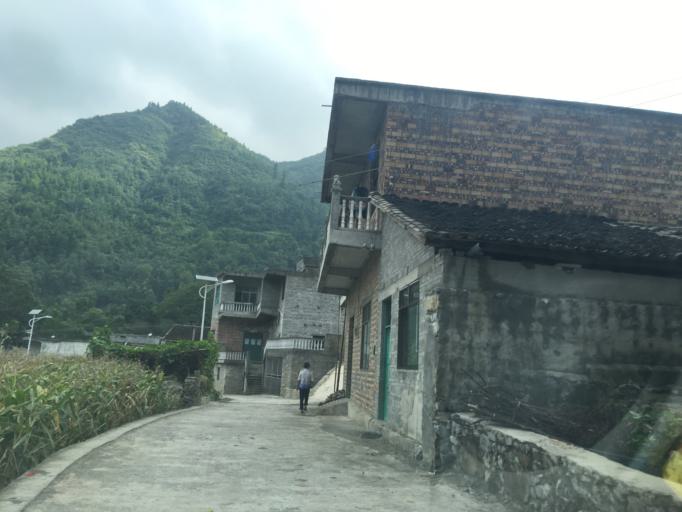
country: CN
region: Guangxi Zhuangzu Zizhiqu
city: Xinzhou
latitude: 25.0748
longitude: 105.7267
